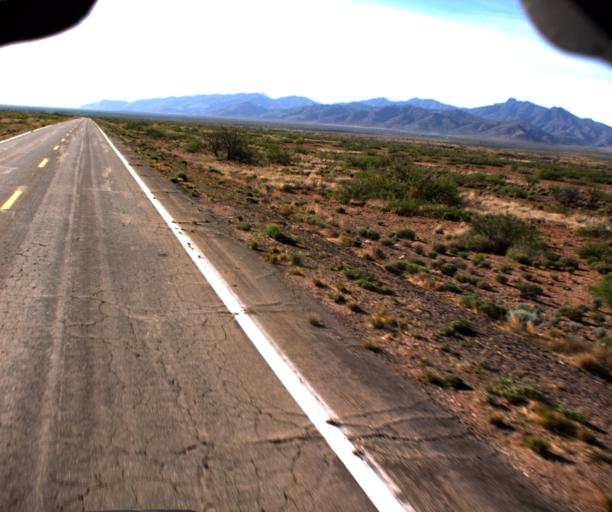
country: US
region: Arizona
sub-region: Cochise County
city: Willcox
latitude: 32.3793
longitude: -109.6475
